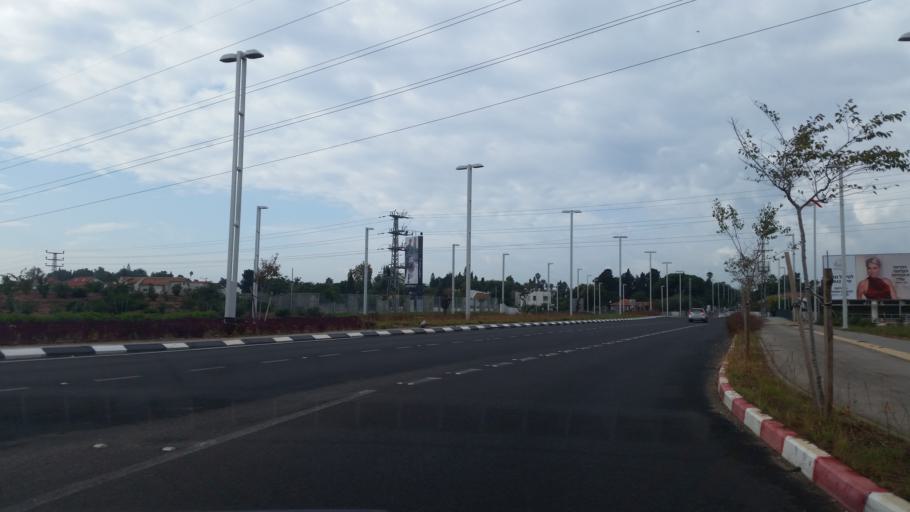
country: IL
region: Tel Aviv
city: Kefar Shemaryahu
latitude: 32.1792
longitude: 34.8242
